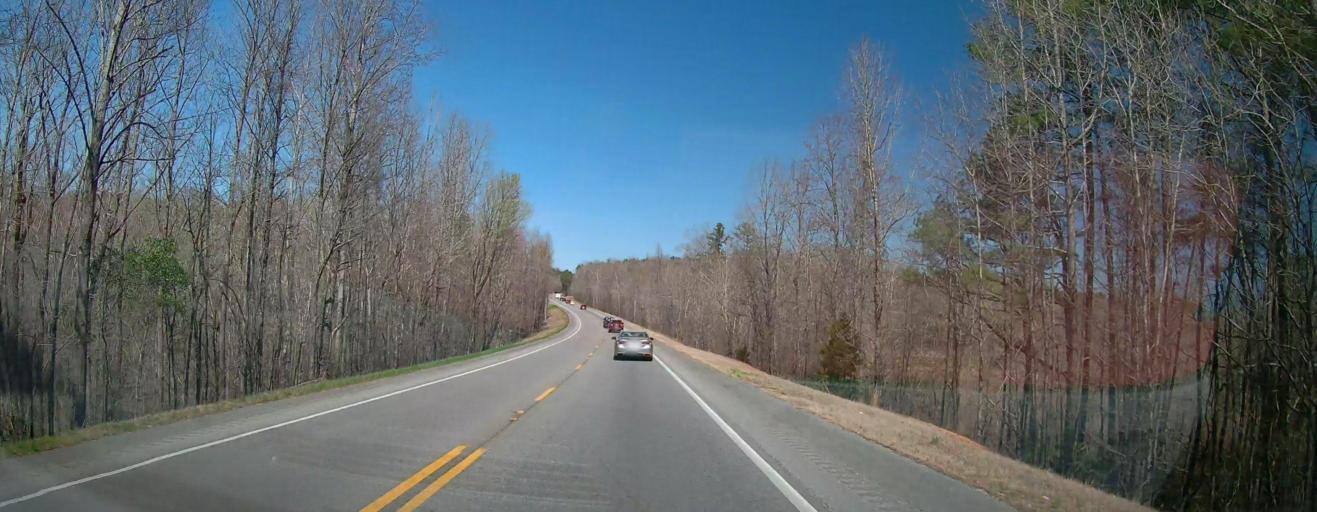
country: US
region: Alabama
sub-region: Calhoun County
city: Ohatchee
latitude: 33.7895
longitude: -86.0354
